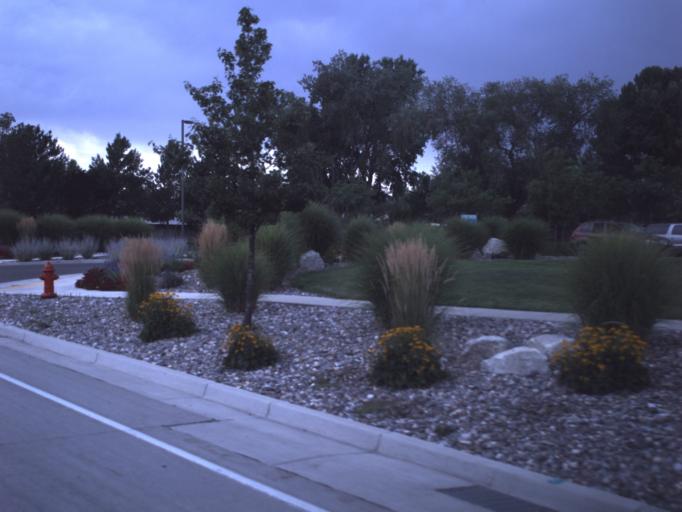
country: US
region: Utah
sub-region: Salt Lake County
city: White City
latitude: 40.5663
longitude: -111.8722
